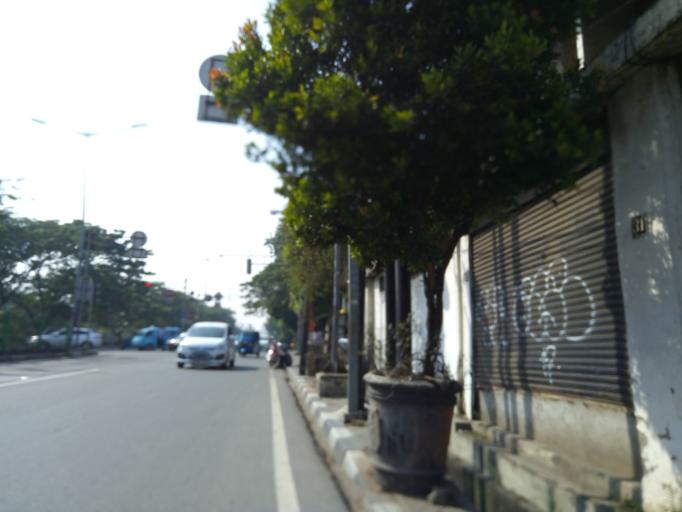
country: ID
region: Jakarta Raya
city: Jakarta
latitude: -6.2063
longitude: 106.8380
